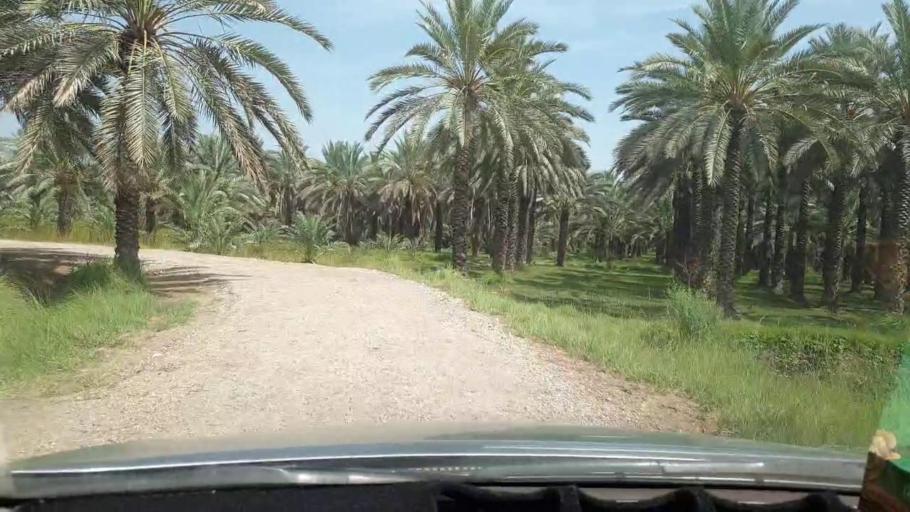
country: PK
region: Sindh
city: Khairpur
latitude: 27.4698
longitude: 68.7483
